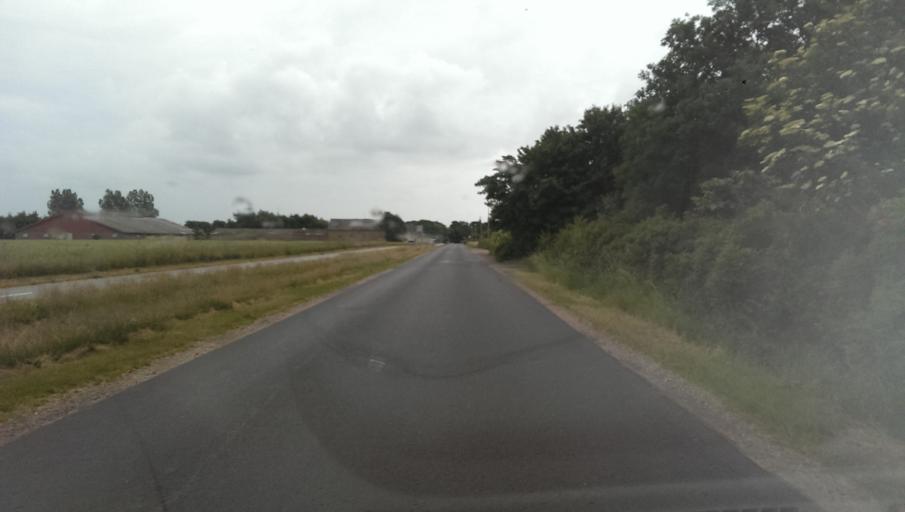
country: DK
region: South Denmark
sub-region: Esbjerg Kommune
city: Bramming
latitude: 55.4397
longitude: 8.7213
